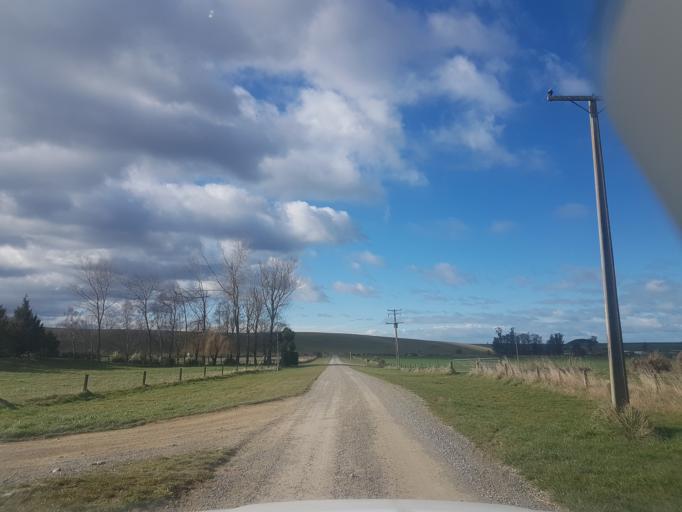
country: NZ
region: Canterbury
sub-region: Timaru District
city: Pleasant Point
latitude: -44.1883
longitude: 171.1836
